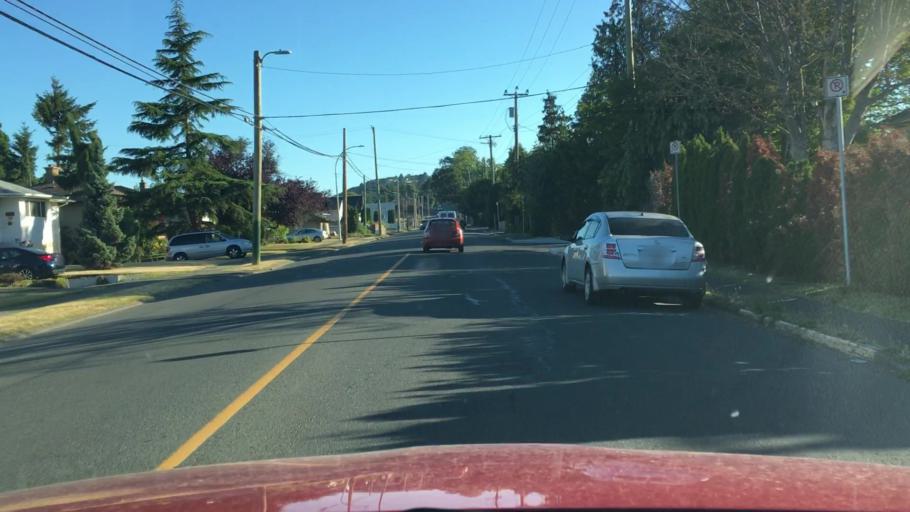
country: CA
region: British Columbia
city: Oak Bay
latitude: 48.4417
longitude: -123.3275
